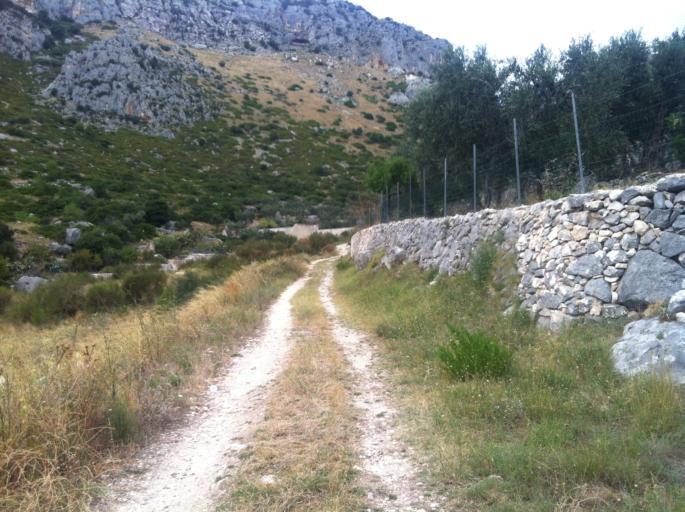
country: IT
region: Apulia
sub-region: Provincia di Foggia
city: Manfredonia
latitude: 41.6676
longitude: 15.9097
